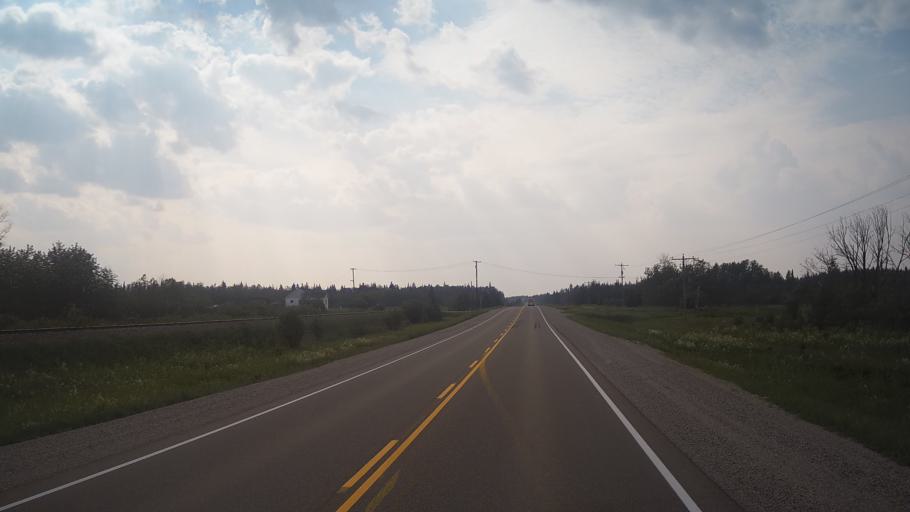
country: CA
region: Ontario
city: Kapuskasing
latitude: 49.5145
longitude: -82.7882
